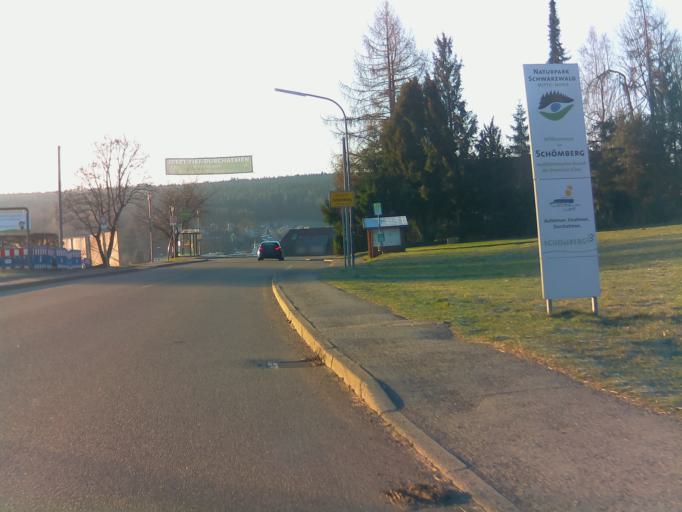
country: DE
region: Baden-Wuerttemberg
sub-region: Karlsruhe Region
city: Schomberg
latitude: 48.7927
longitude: 8.6420
